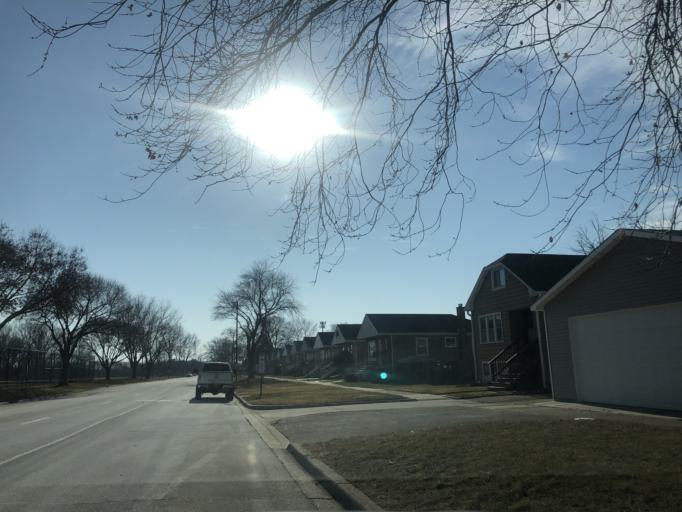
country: US
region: Illinois
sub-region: Cook County
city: Stickney
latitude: 41.8177
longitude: -87.7828
